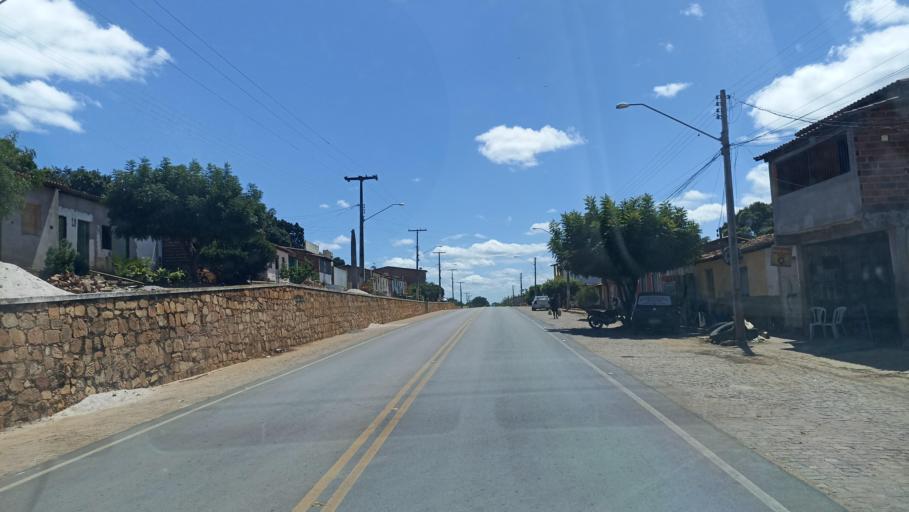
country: BR
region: Bahia
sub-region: Andarai
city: Vera Cruz
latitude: -12.7951
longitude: -41.3279
